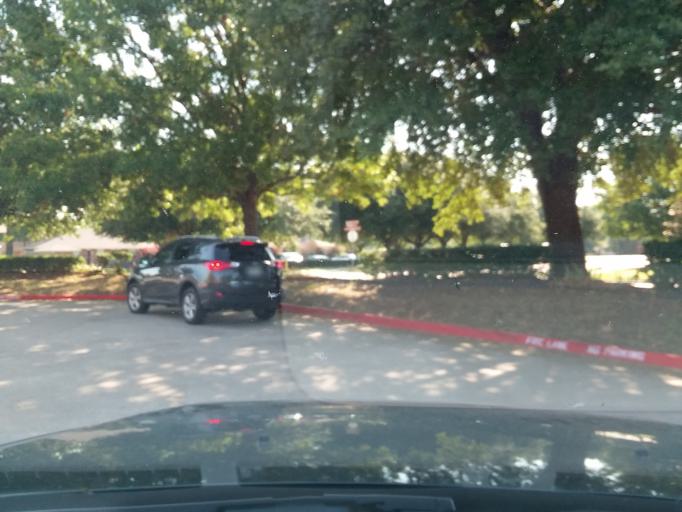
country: US
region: Texas
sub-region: Denton County
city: Flower Mound
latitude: 33.0367
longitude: -97.0637
